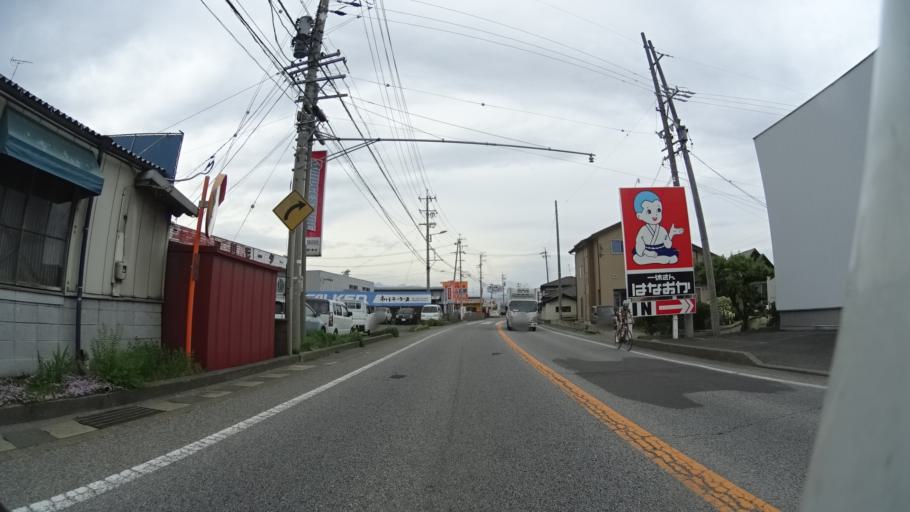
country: JP
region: Nagano
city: Nagano-shi
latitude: 36.5391
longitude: 138.1225
